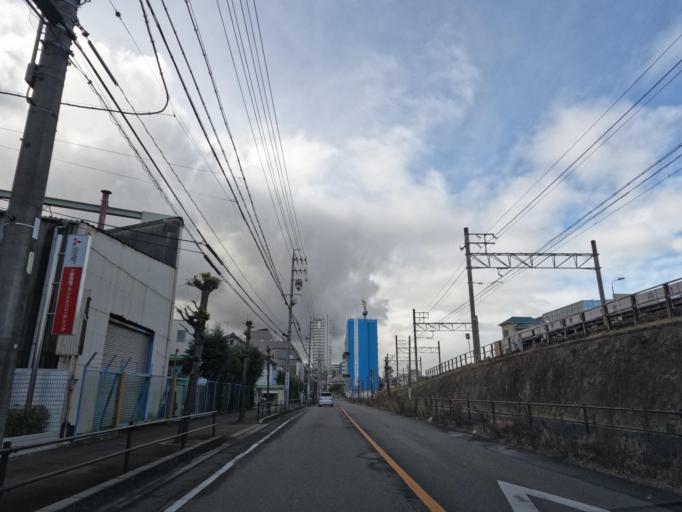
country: JP
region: Aichi
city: Chiryu
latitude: 34.9888
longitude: 137.0126
